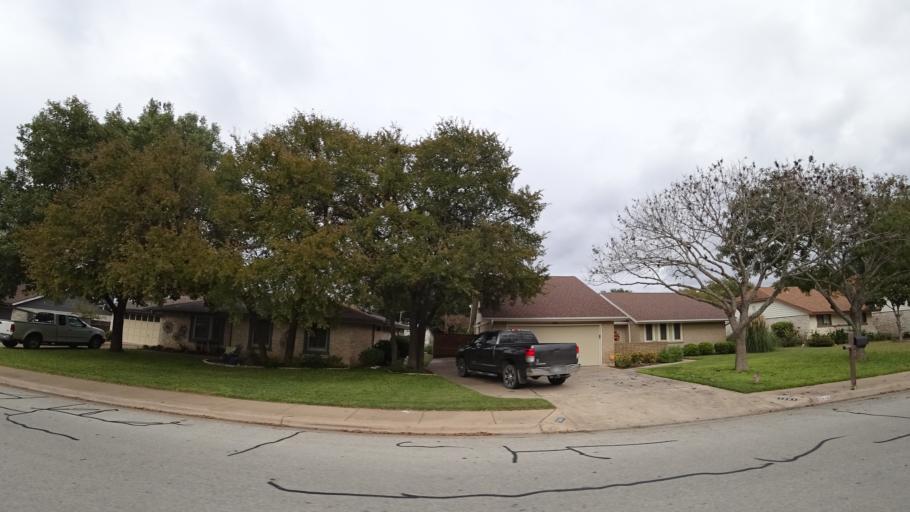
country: US
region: Texas
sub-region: Williamson County
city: Round Rock
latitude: 30.4980
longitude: -97.6970
